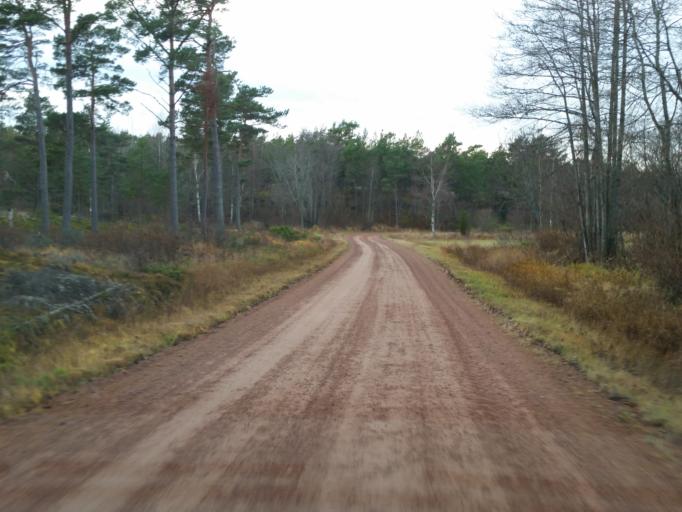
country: AX
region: Alands skaergard
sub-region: Kumlinge
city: Kumlinge
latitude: 60.2686
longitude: 20.8099
